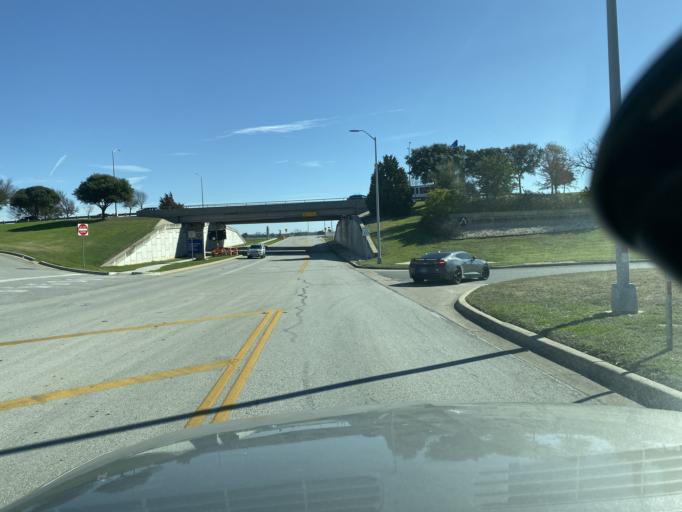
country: US
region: Texas
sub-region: Travis County
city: Hornsby Bend
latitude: 30.2113
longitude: -97.6623
